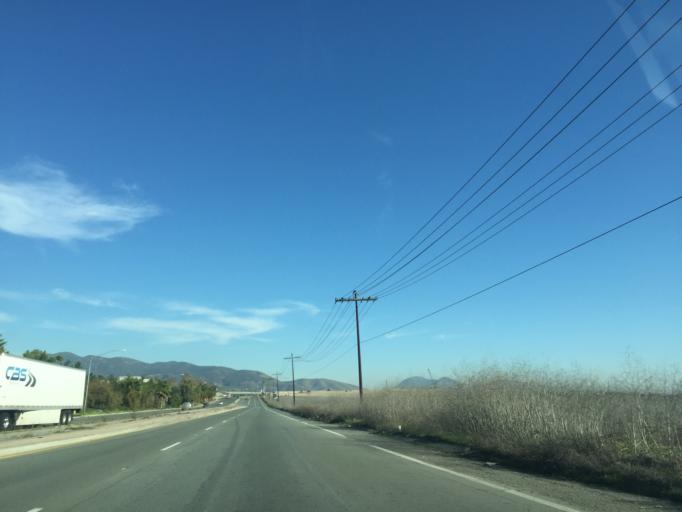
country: MX
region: Baja California
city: Tijuana
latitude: 32.5676
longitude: -116.9589
